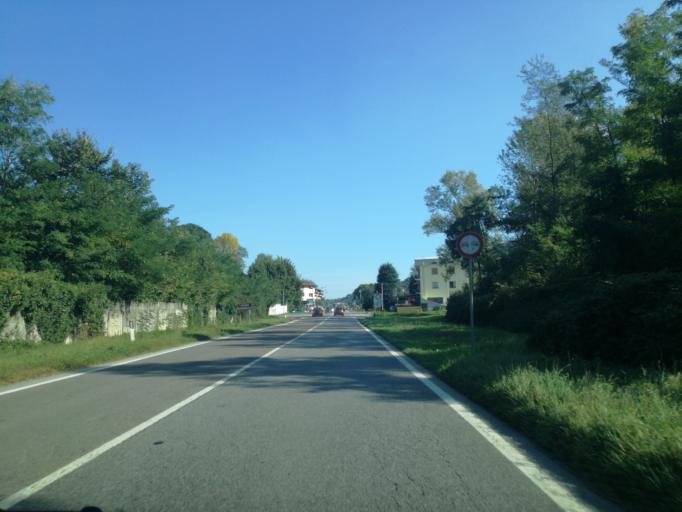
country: IT
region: Lombardy
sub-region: Provincia di Bergamo
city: Caprino
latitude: 45.7340
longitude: 9.4896
